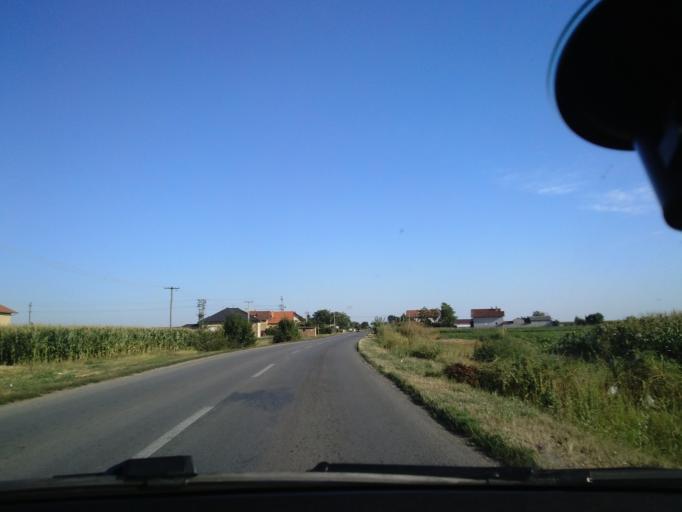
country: RS
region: Autonomna Pokrajina Vojvodina
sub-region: Zapadnobacki Okrug
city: Sombor
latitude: 45.7107
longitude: 19.1629
